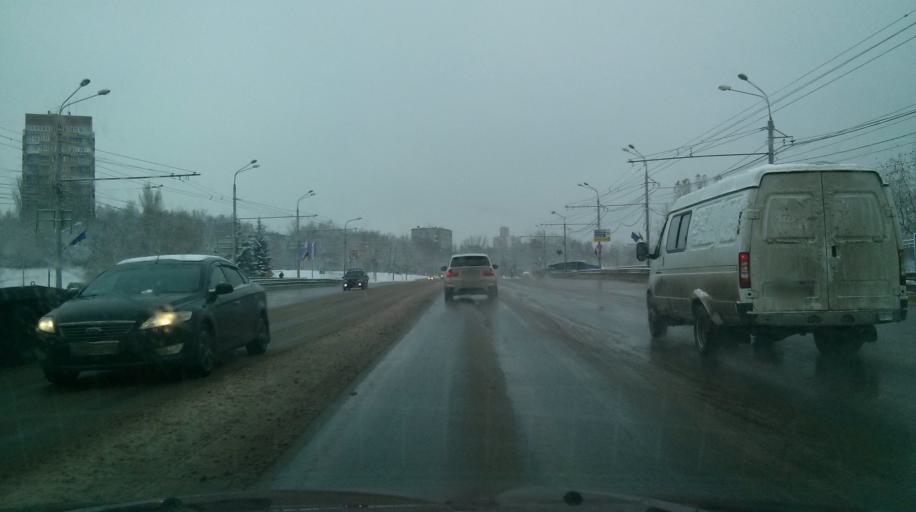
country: RU
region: Nizjnij Novgorod
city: Nizhniy Novgorod
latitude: 56.2449
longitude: 43.9652
